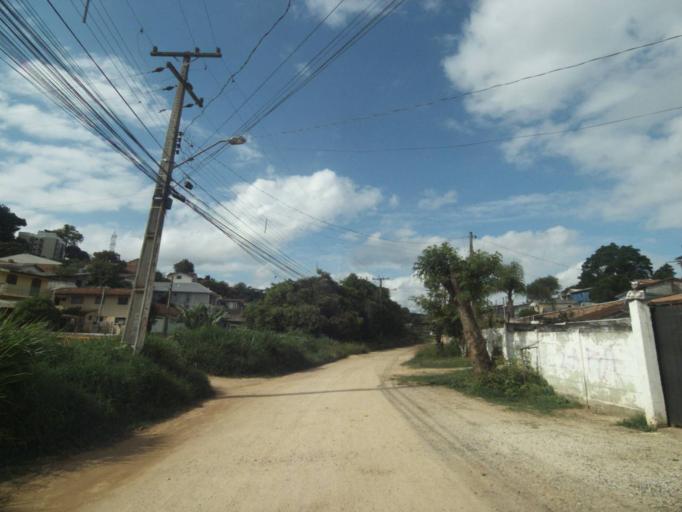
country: BR
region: Parana
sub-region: Curitiba
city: Curitiba
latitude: -25.3805
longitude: -49.3010
